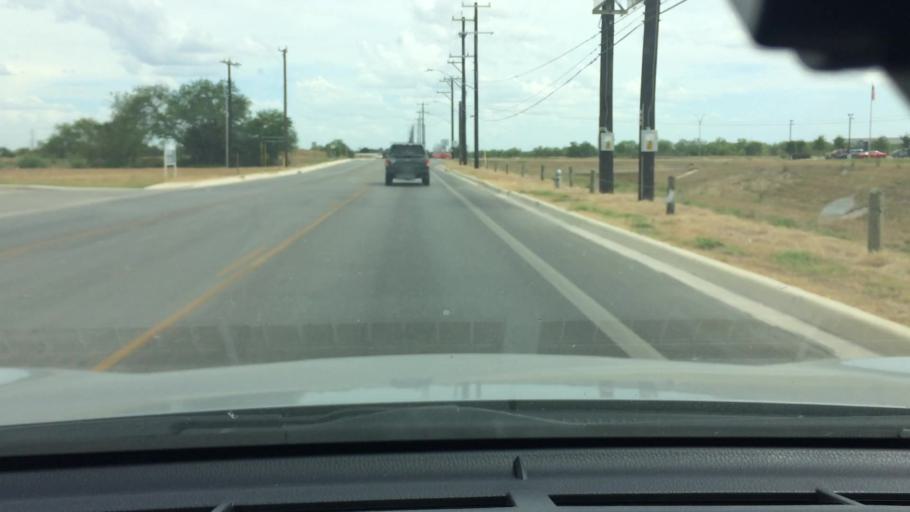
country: US
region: Texas
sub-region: Bexar County
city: China Grove
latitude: 29.3478
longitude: -98.4286
